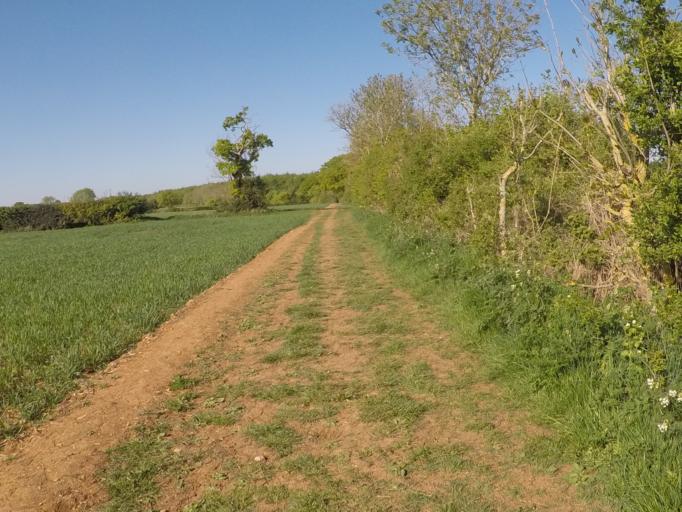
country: GB
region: England
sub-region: Oxfordshire
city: Stonesfield
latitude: 51.8652
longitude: -1.4356
